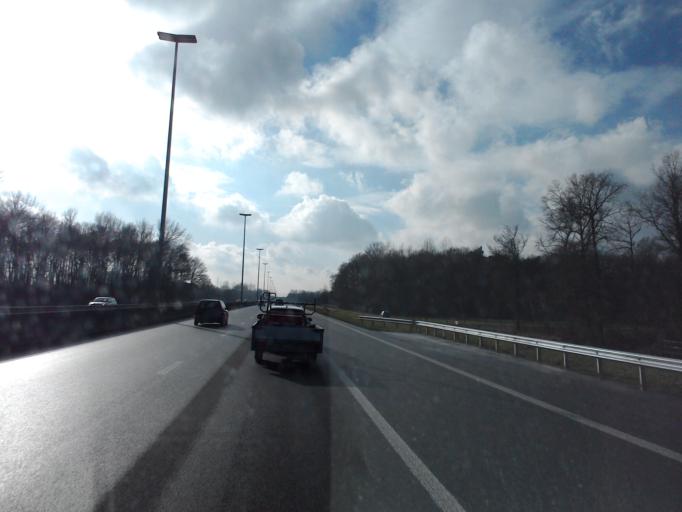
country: BE
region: Flanders
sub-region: Provincie Antwerpen
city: Zandhoven
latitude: 51.2300
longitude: 4.6581
